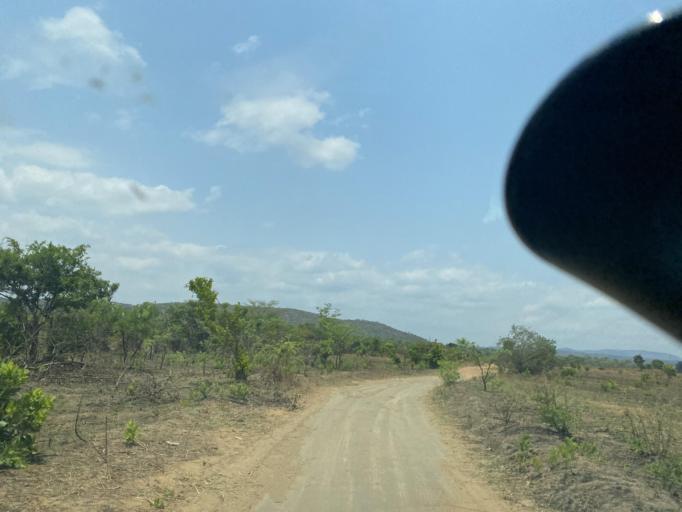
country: ZM
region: Lusaka
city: Chongwe
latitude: -15.5158
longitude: 28.8877
